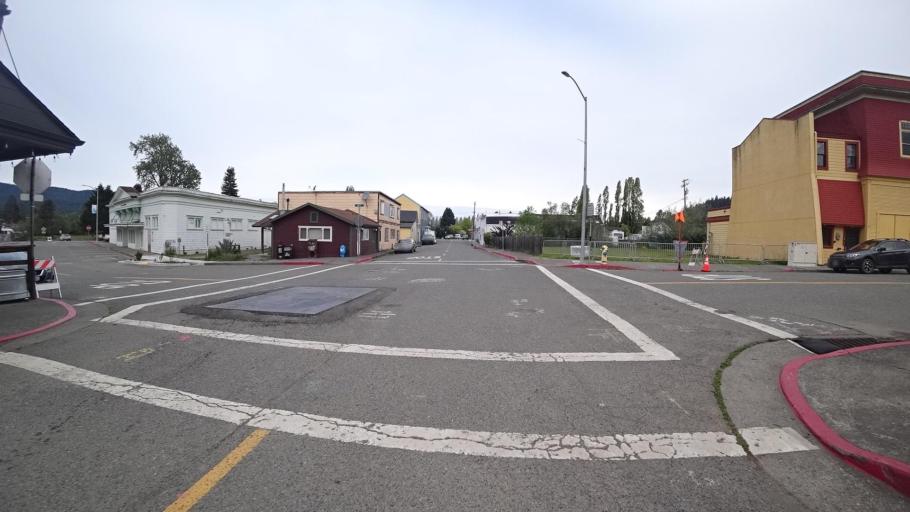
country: US
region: California
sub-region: Humboldt County
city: Blue Lake
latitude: 40.8805
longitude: -123.9890
